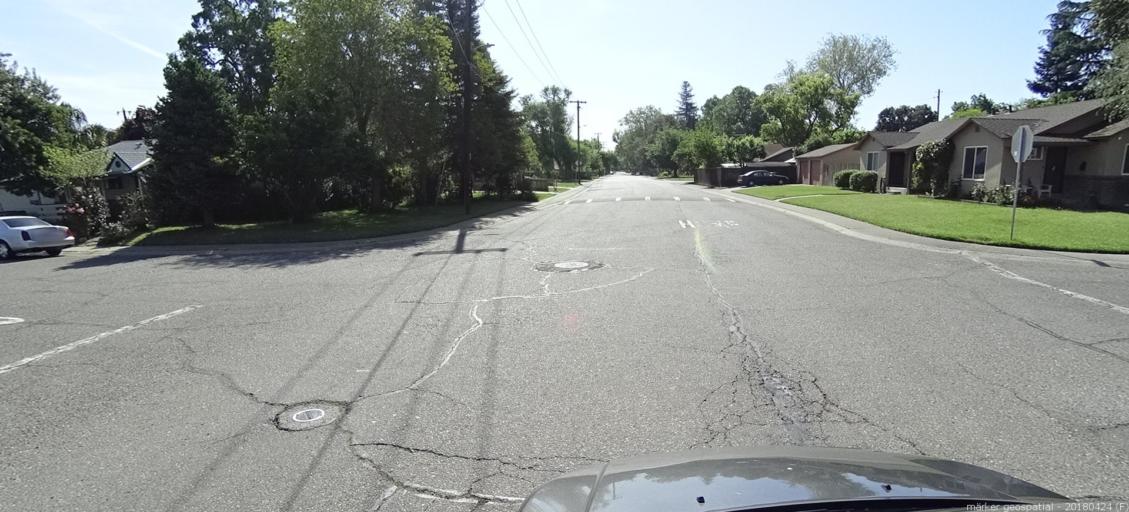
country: US
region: California
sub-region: Yolo County
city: West Sacramento
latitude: 38.5703
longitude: -121.5298
